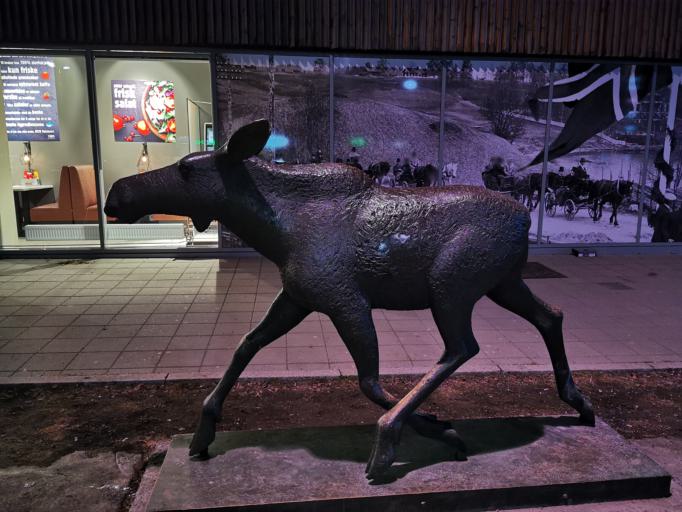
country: NO
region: Akershus
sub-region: Eidsvoll
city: Raholt
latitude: 60.2811
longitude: 11.1741
